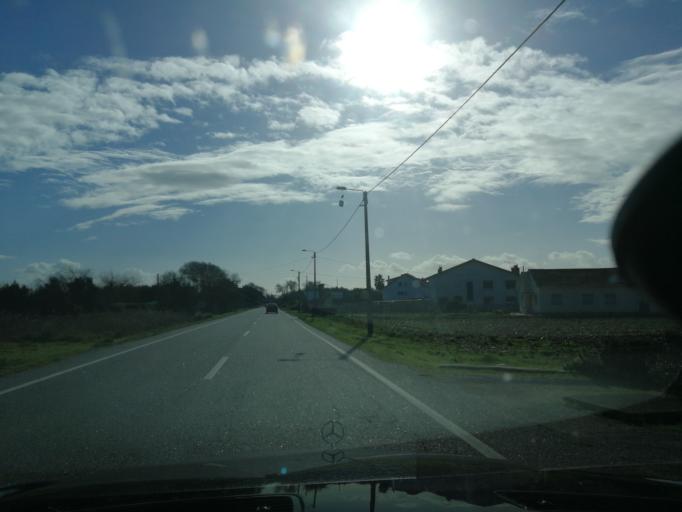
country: PT
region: Aveiro
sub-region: Estarreja
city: Pardilho
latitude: 40.8226
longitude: -8.6681
